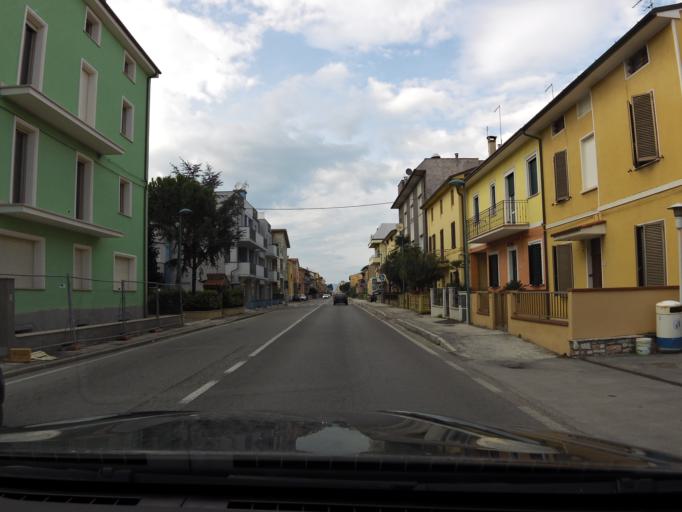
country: IT
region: The Marches
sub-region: Provincia di Macerata
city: Porto Potenza Picena
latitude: 43.3629
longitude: 13.6959
